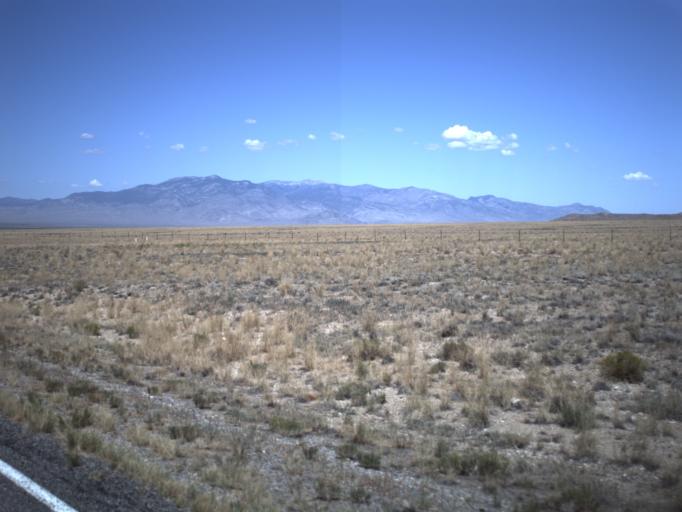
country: US
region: Nevada
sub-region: White Pine County
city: McGill
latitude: 39.0422
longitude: -113.8538
